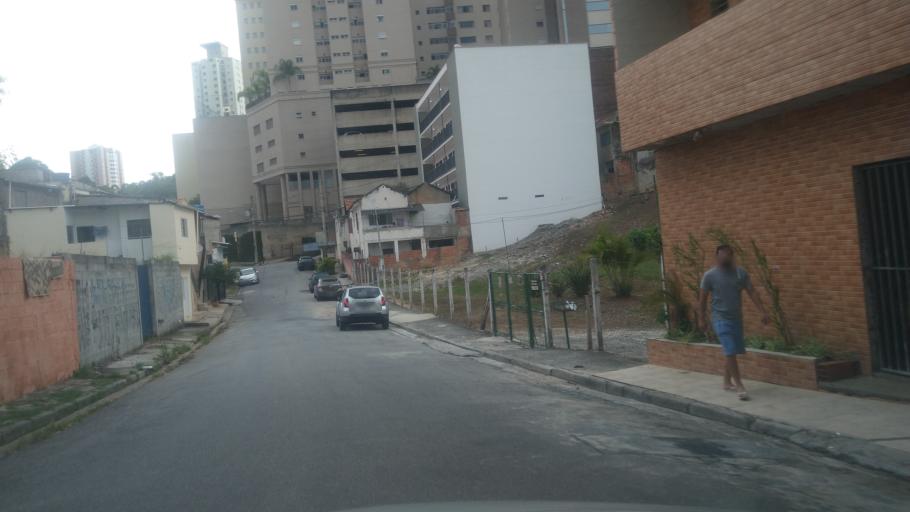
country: BR
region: Sao Paulo
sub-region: Sao Paulo
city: Sao Paulo
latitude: -23.4862
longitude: -46.6262
